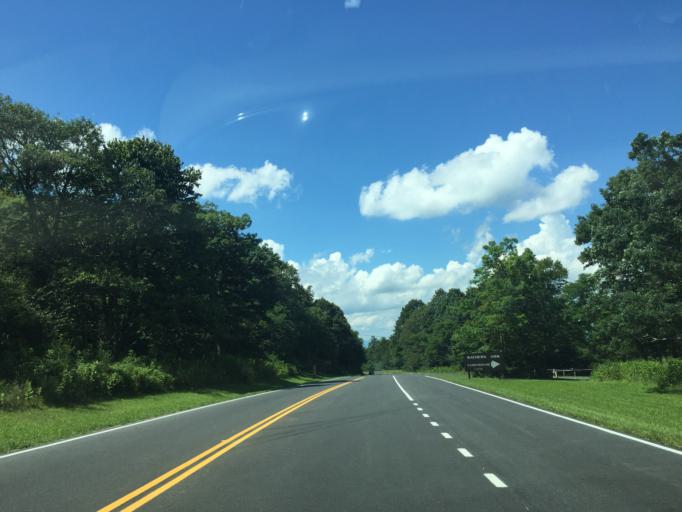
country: US
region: Virginia
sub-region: Rappahannock County
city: Washington
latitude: 38.7511
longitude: -78.2931
